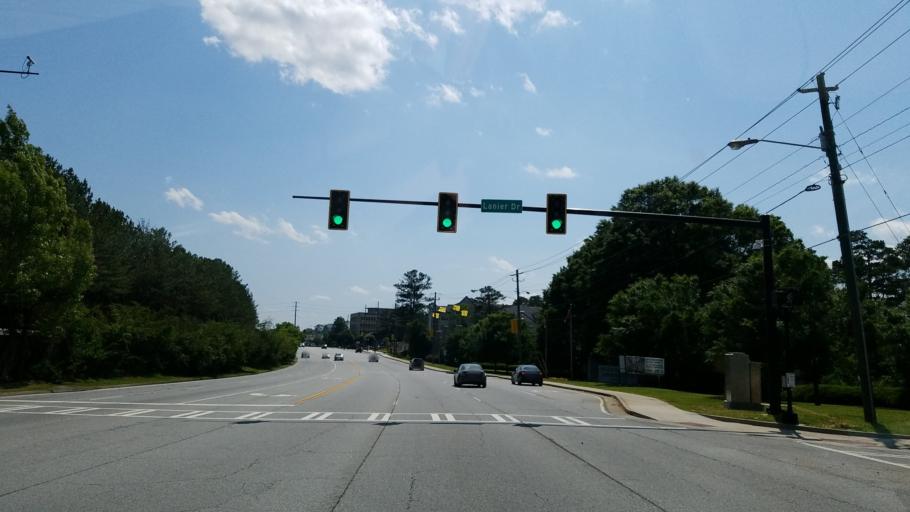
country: US
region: Georgia
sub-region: DeKalb County
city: North Atlanta
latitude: 33.8740
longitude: -84.3303
